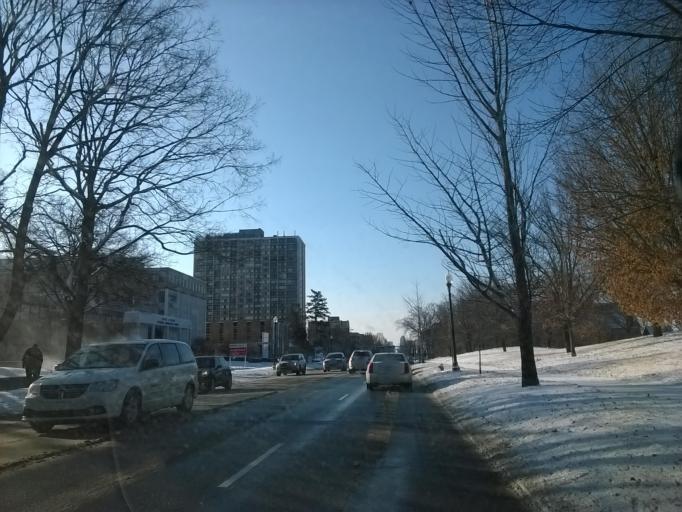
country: US
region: Indiana
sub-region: Marion County
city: Broad Ripple
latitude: 39.8277
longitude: -86.1569
